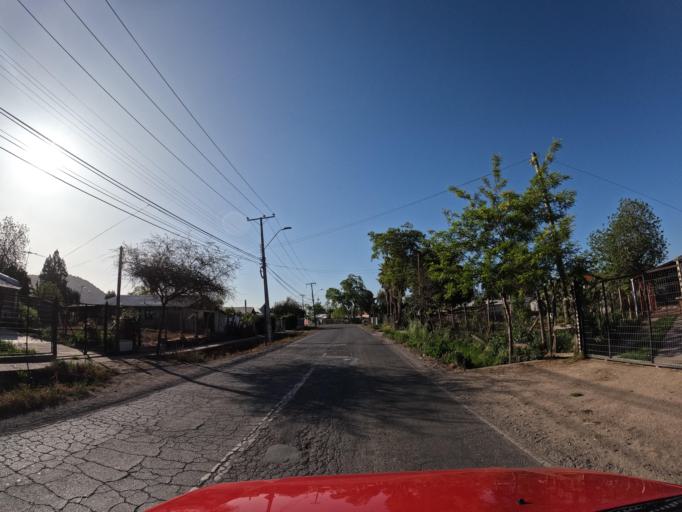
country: CL
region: O'Higgins
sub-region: Provincia de Colchagua
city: Santa Cruz
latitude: -34.7120
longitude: -71.2908
